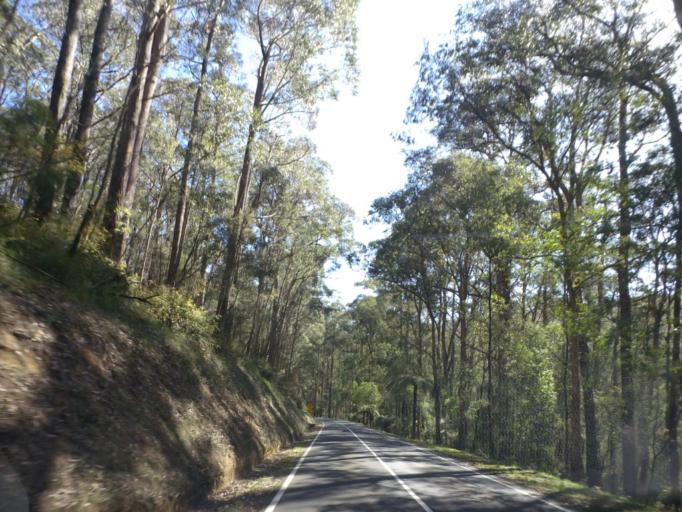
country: AU
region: Victoria
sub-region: Yarra Ranges
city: Millgrove
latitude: -37.8762
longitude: 145.7866
